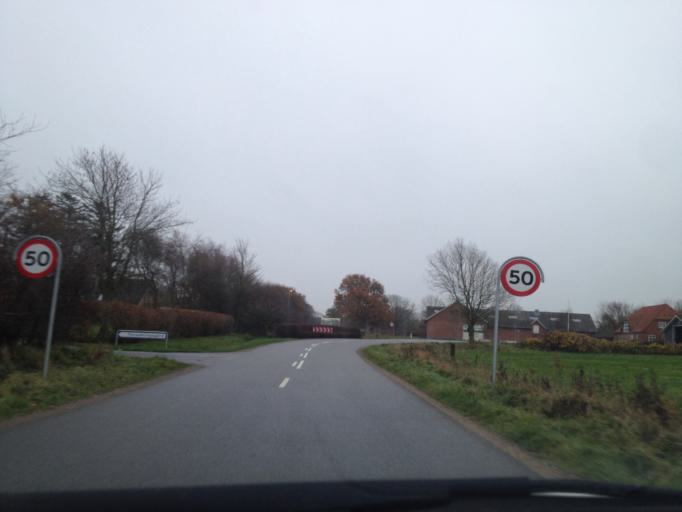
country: DK
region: South Denmark
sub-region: Tonder Kommune
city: Sherrebek
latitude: 55.0861
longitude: 8.7245
